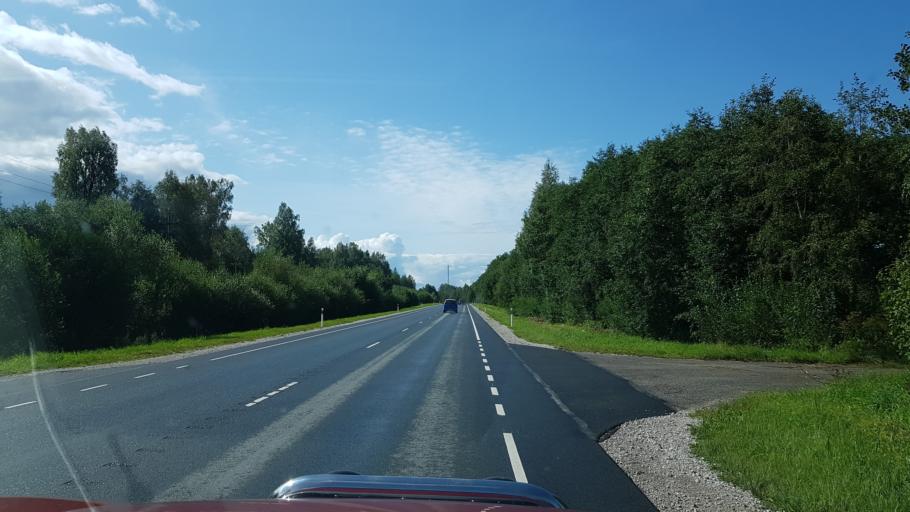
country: EE
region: Harju
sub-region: Nissi vald
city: Turba
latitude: 58.8942
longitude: 24.0998
